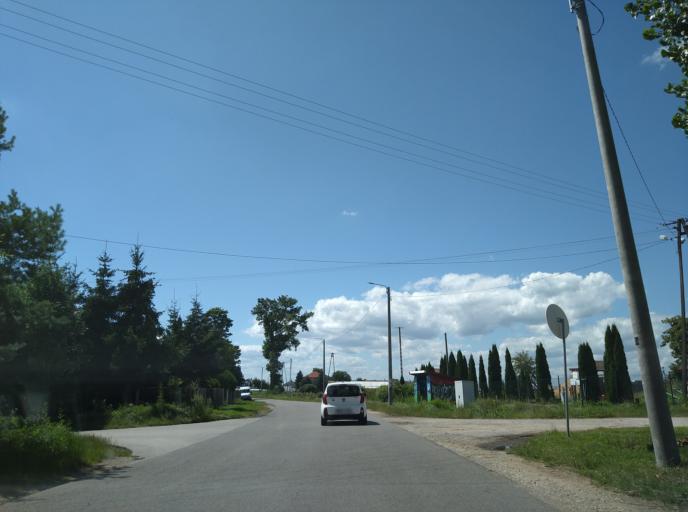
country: PL
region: Masovian Voivodeship
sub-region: Powiat bialobrzeski
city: Bialobrzegi
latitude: 51.6706
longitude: 20.8876
